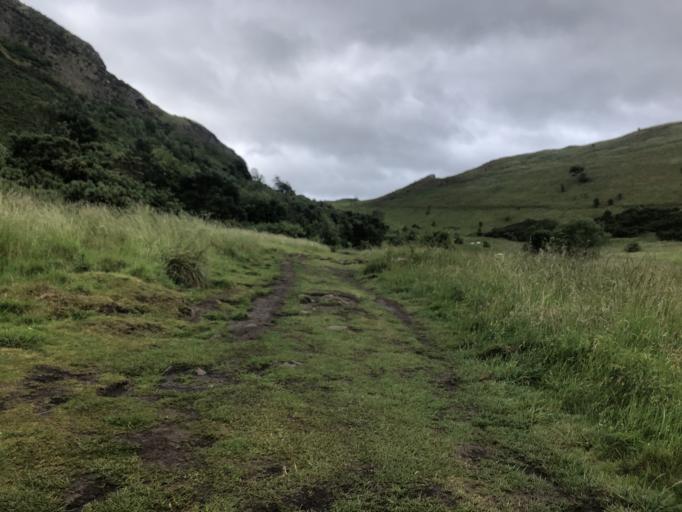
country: GB
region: Scotland
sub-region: West Lothian
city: Seafield
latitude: 55.9467
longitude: -3.1652
